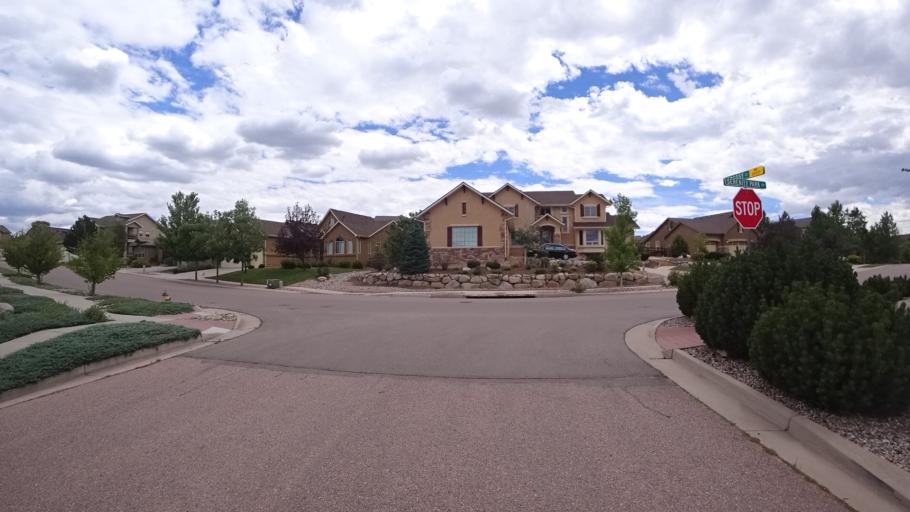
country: US
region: Colorado
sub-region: El Paso County
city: Gleneagle
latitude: 39.0187
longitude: -104.8058
